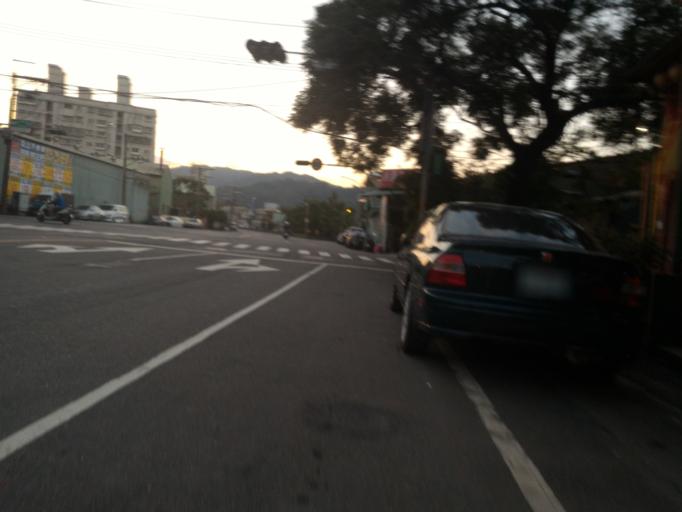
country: TW
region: Taipei
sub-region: Taipei
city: Banqiao
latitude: 24.9742
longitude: 121.4189
